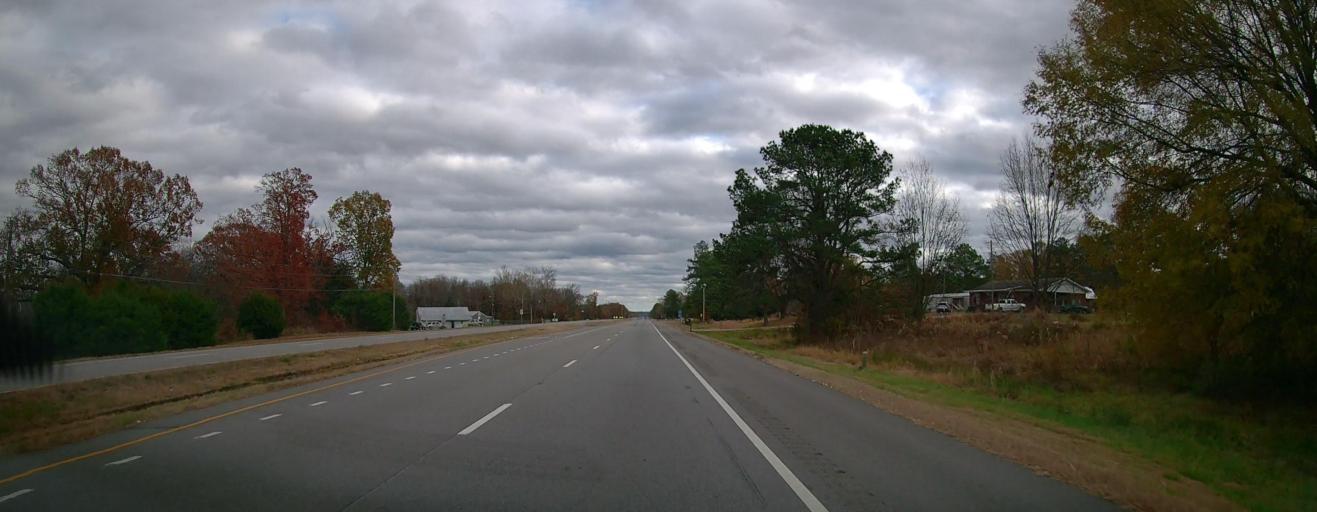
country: US
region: Alabama
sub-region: Lawrence County
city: Town Creek
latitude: 34.6637
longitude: -87.5487
